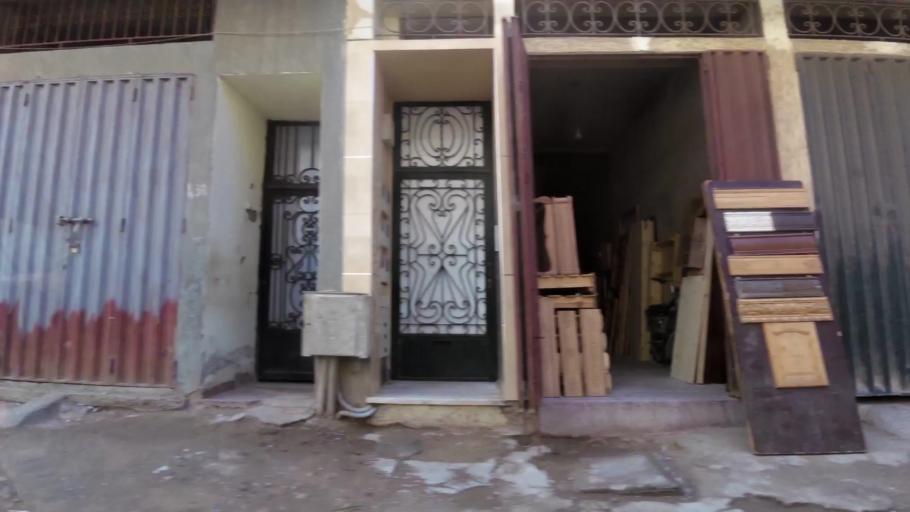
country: MA
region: Grand Casablanca
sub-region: Nouaceur
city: Dar Bouazza
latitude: 33.5313
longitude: -7.7338
